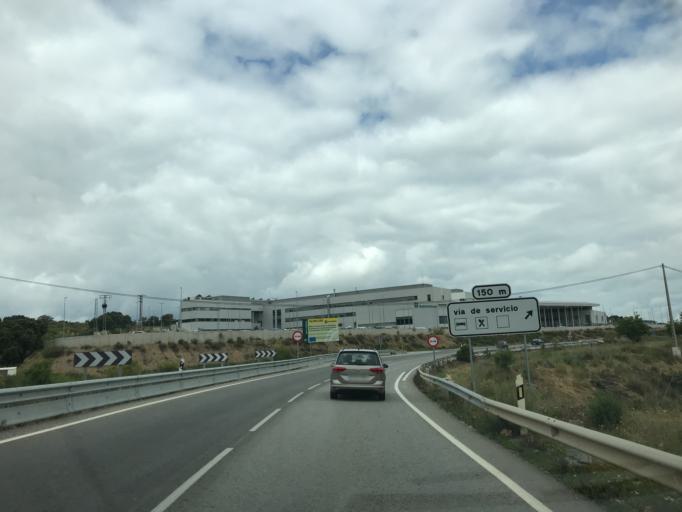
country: ES
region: Andalusia
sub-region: Provincia de Malaga
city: Ronda
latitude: 36.7205
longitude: -5.1440
